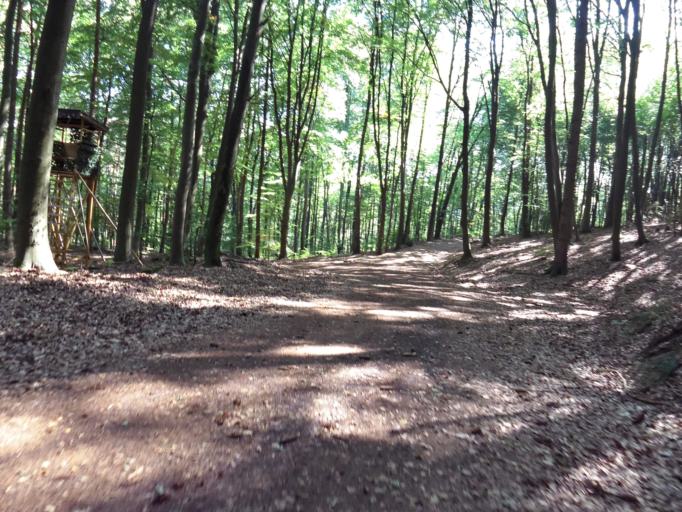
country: DE
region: Rheinland-Pfalz
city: Neidenfels
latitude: 49.4252
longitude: 8.0572
